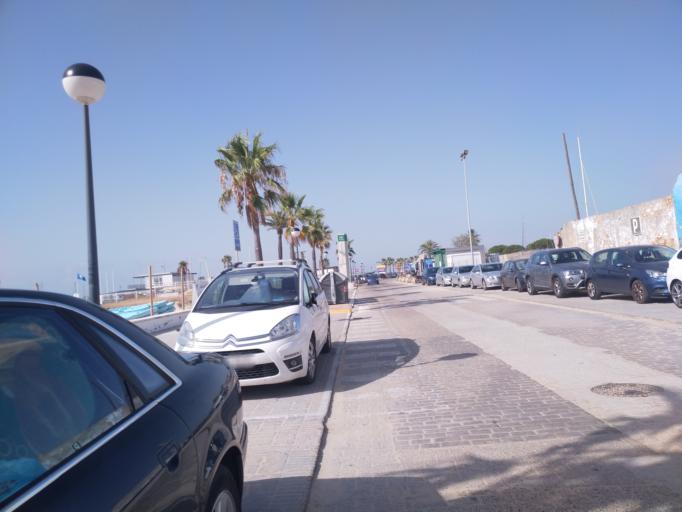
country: ES
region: Andalusia
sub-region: Provincia de Cadiz
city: Chiclana de la Frontera
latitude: 36.3938
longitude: -6.2092
